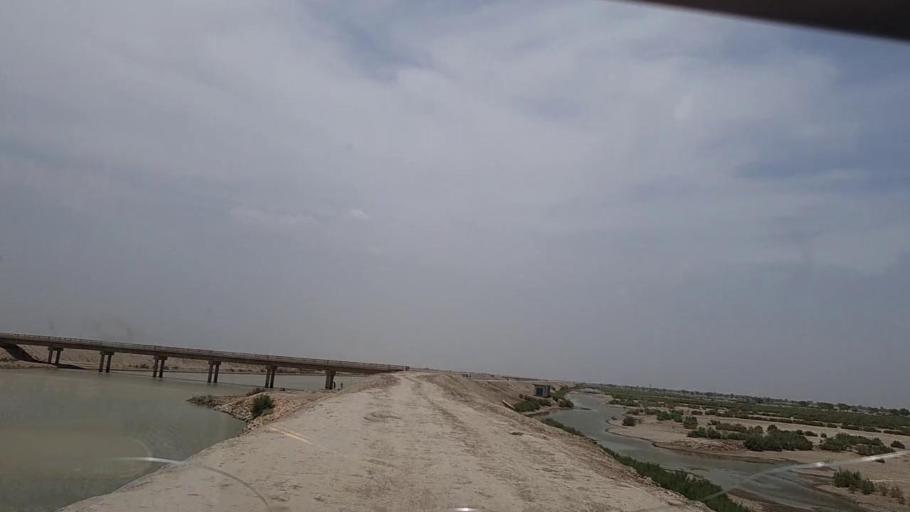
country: PK
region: Sindh
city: Bhan
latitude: 26.5095
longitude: 67.6256
